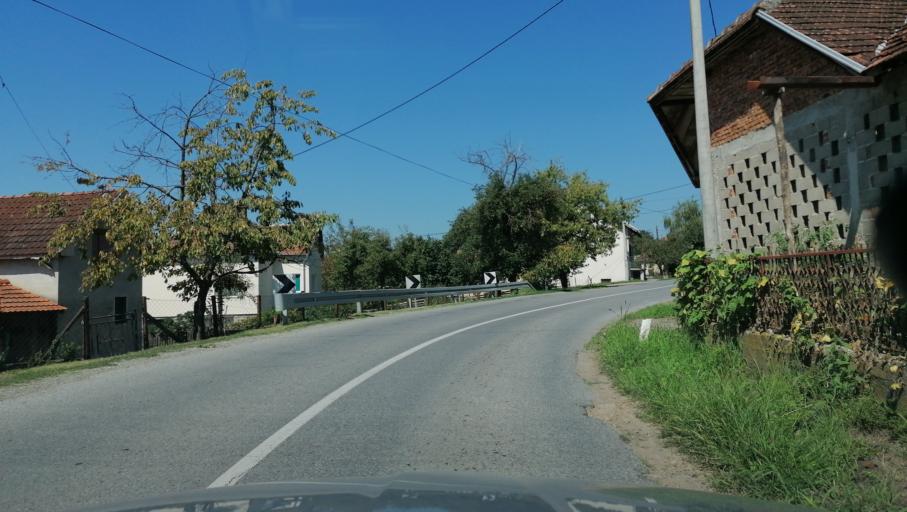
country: RS
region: Central Serbia
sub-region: Raski Okrug
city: Vrnjacka Banja
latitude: 43.6882
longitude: 20.8713
